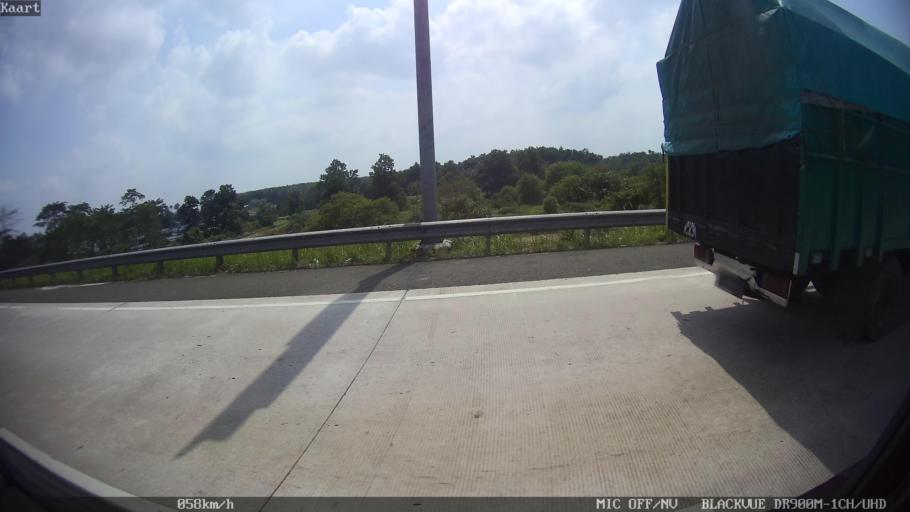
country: ID
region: Lampung
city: Kedaton
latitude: -5.3536
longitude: 105.3233
